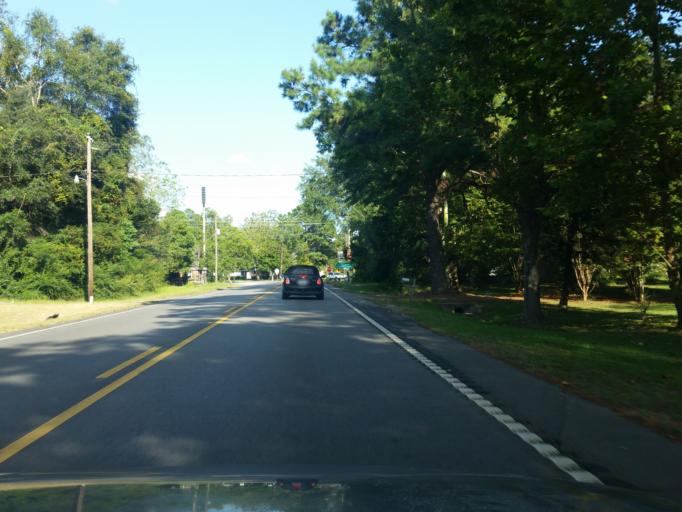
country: US
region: Alabama
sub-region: Mobile County
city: Theodore
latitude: 30.5013
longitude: -88.1125
